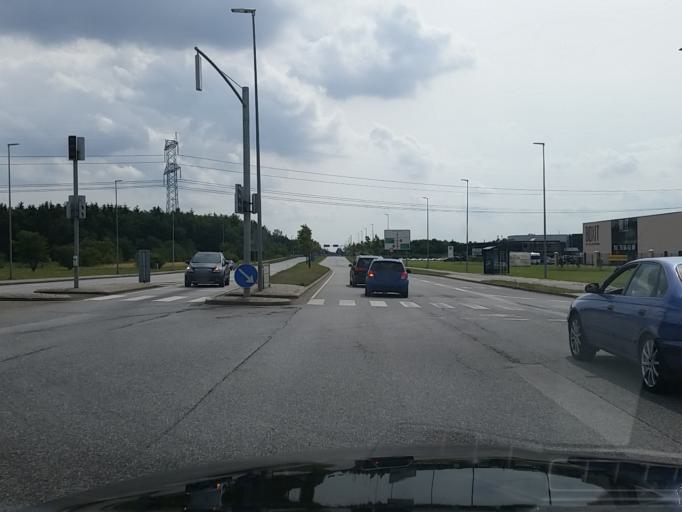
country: DK
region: South Denmark
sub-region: Kolding Kommune
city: Kolding
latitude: 55.5328
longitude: 9.4688
